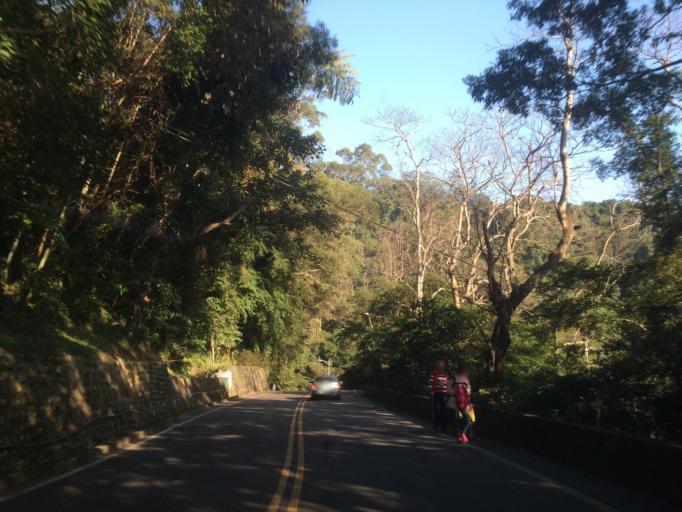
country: TW
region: Taiwan
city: Daxi
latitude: 24.8127
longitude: 121.2564
